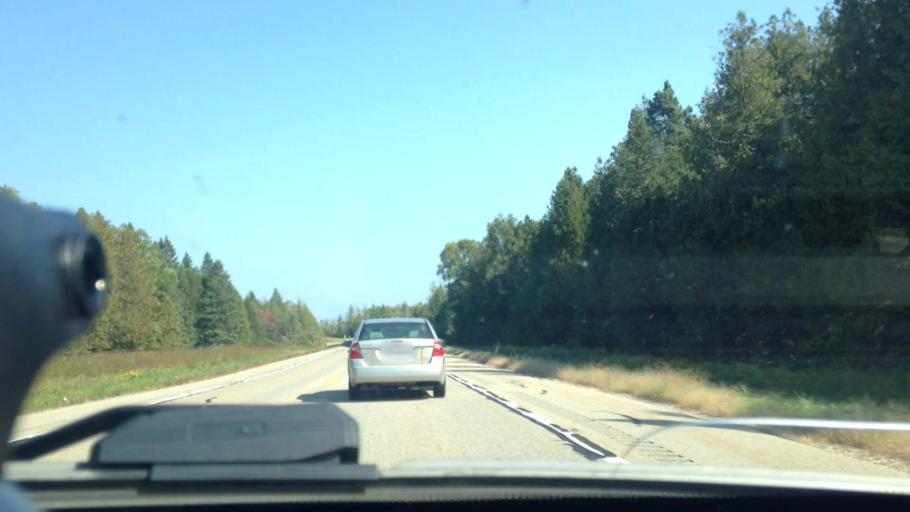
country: US
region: Michigan
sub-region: Luce County
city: Newberry
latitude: 46.3036
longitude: -85.2328
